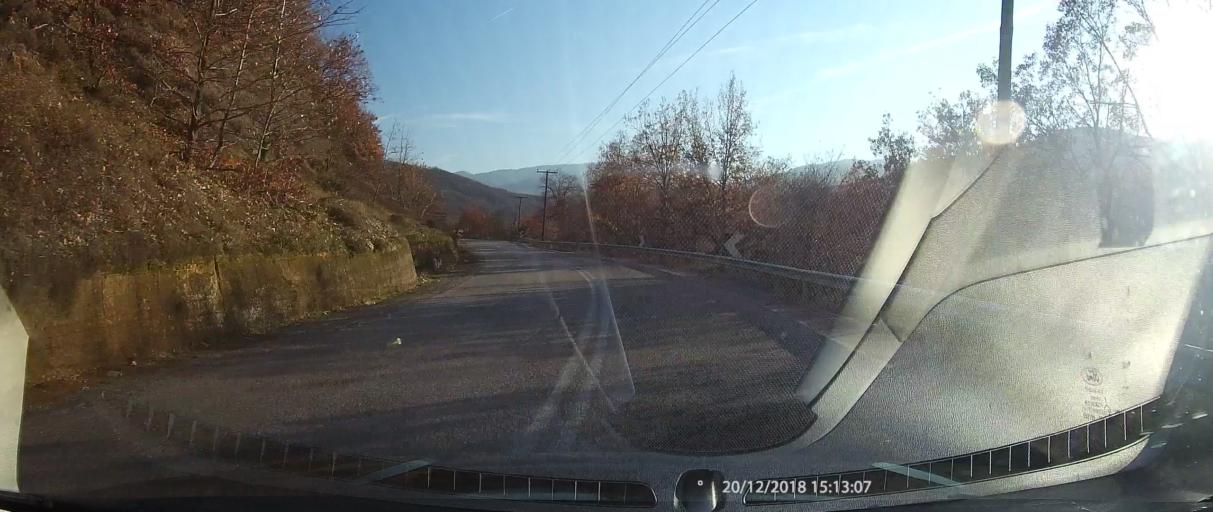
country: GR
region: Central Greece
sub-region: Nomos Fthiotidos
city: Makrakomi
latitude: 38.9358
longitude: 21.9647
